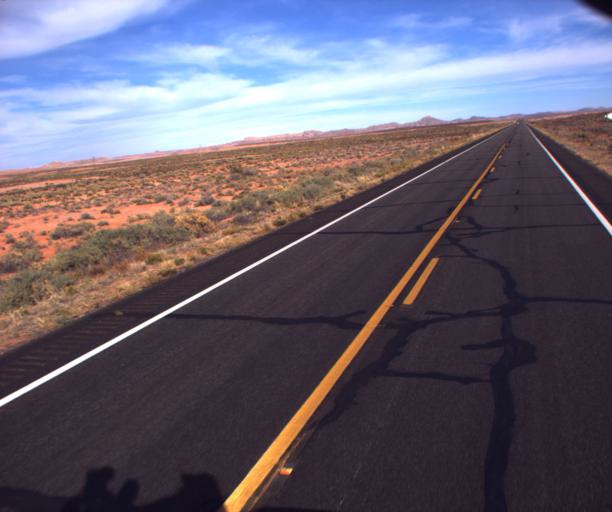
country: US
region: Arizona
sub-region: Apache County
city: Many Farms
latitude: 36.9390
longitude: -109.6910
